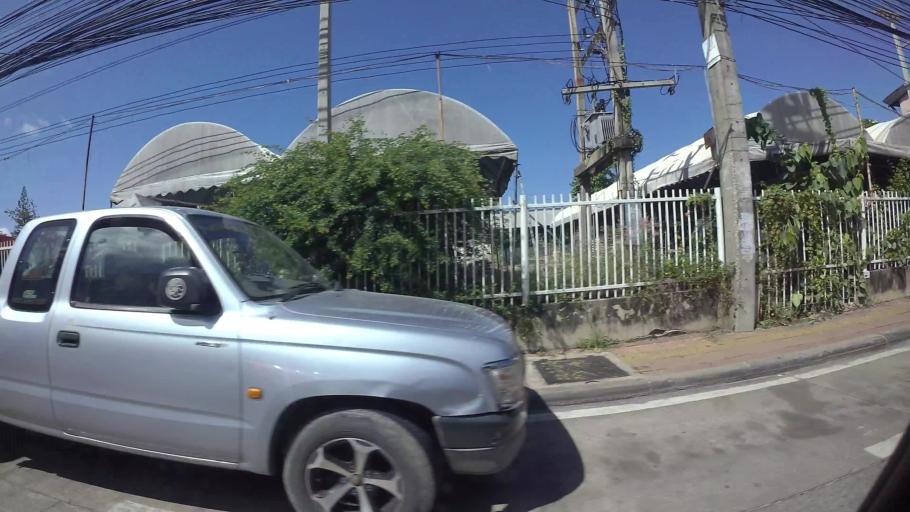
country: TH
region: Chon Buri
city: Phatthaya
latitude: 12.9324
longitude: 100.8987
